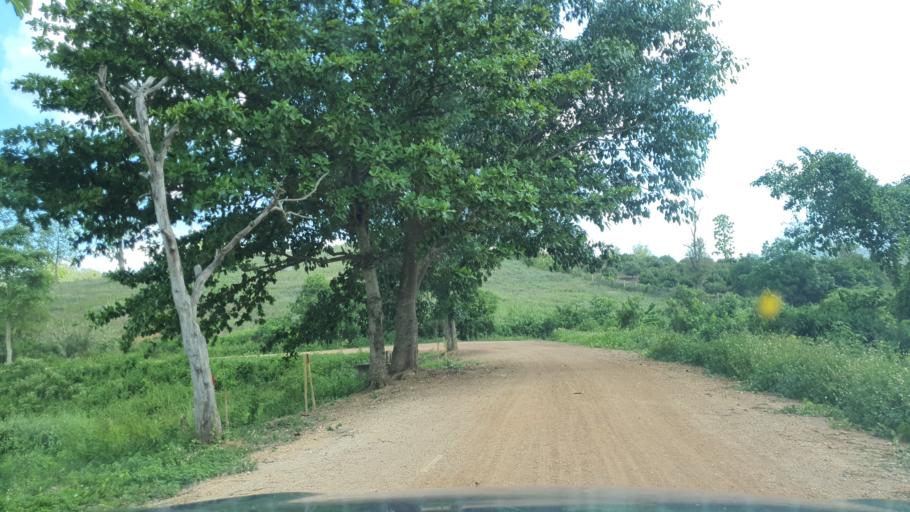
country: TH
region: Chiang Mai
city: Mae Taeng
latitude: 19.0926
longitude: 99.0777
